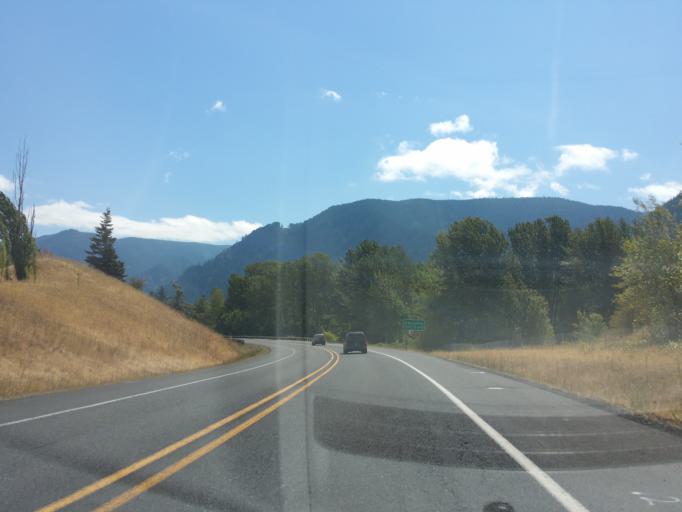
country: US
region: Oregon
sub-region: Hood River County
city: Cascade Locks
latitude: 45.6408
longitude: -121.9822
